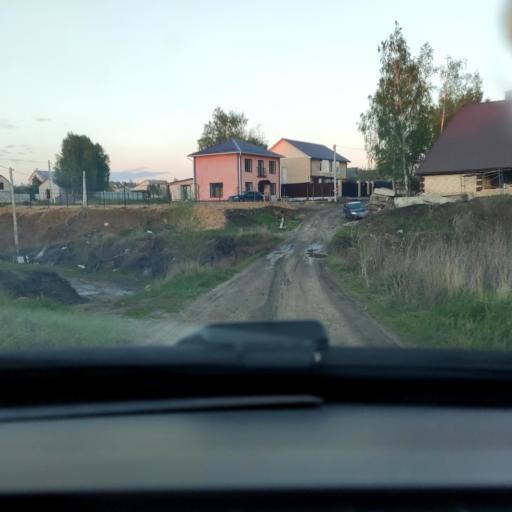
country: RU
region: Voronezj
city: Novaya Usman'
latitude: 51.6549
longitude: 39.4243
